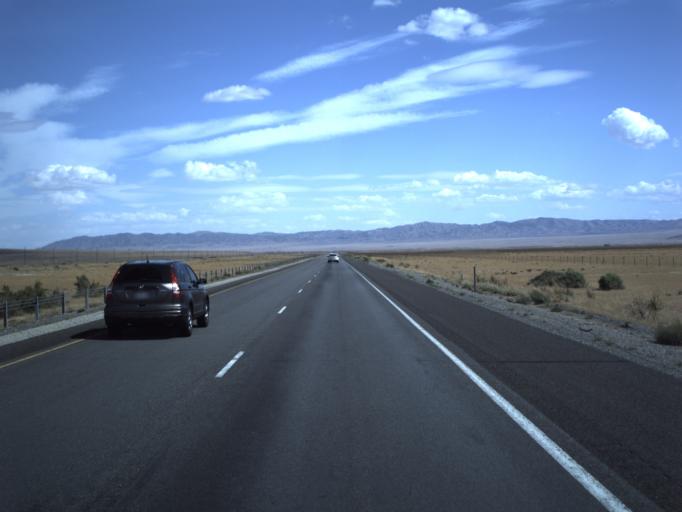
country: US
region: Utah
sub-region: Tooele County
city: Grantsville
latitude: 40.7257
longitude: -113.1950
